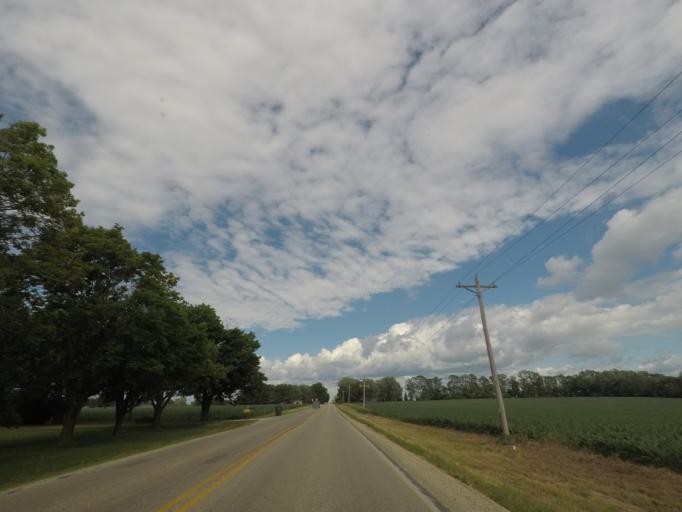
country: US
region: Wisconsin
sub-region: Rock County
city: Janesville
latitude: 42.7013
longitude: -89.1303
